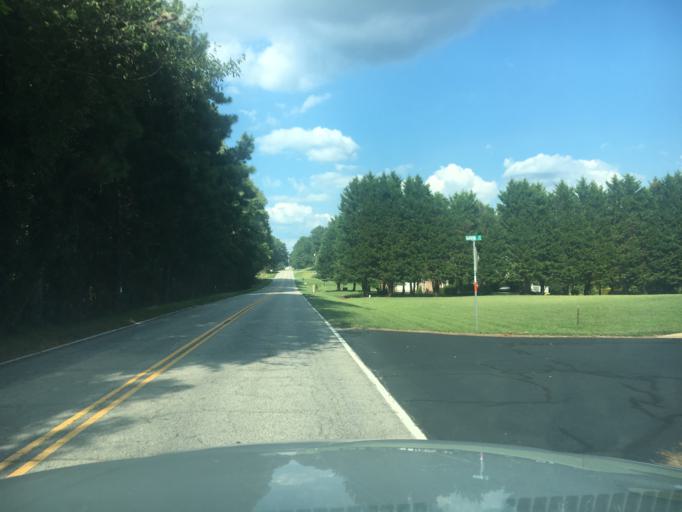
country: US
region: South Carolina
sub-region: Anderson County
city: Pendleton
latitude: 34.6815
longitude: -82.7519
